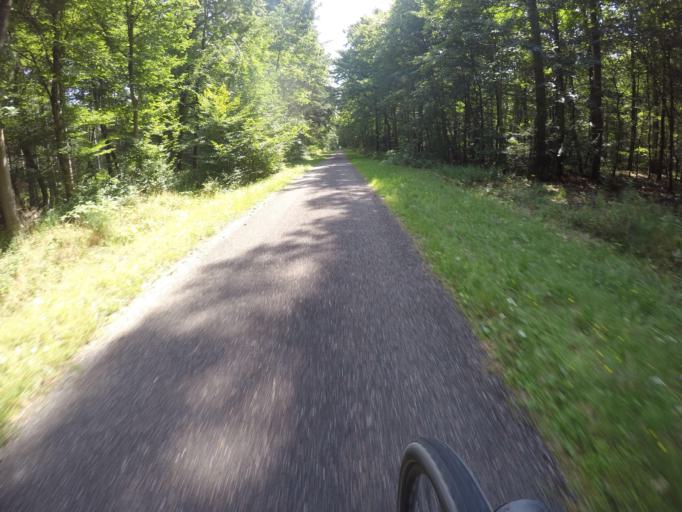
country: DE
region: Baden-Wuerttemberg
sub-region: Karlsruhe Region
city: Hambrucken
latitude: 49.2172
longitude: 8.5739
